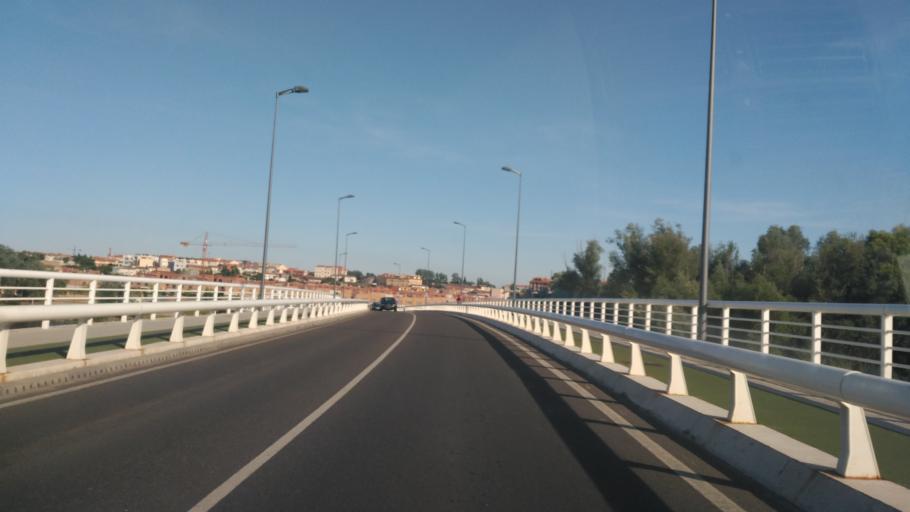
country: ES
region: Castille and Leon
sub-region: Provincia de Zamora
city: Zamora
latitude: 41.4957
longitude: -5.7585
